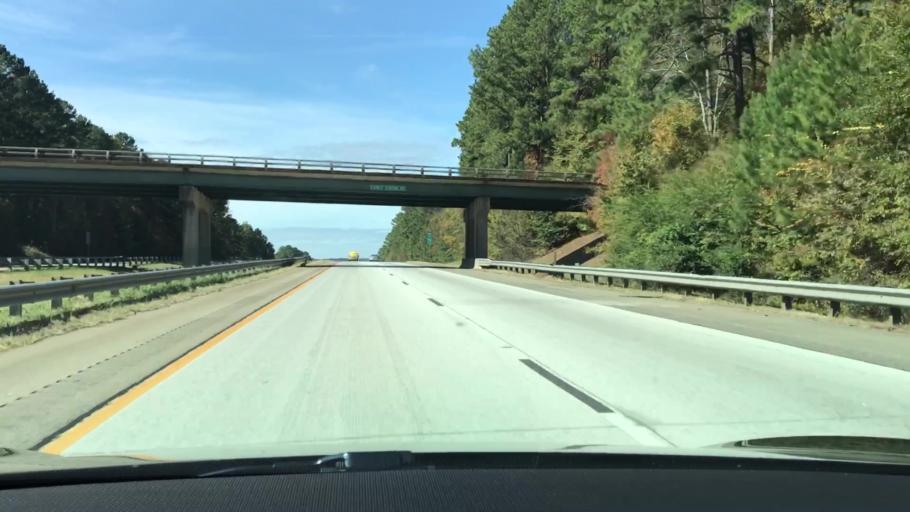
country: US
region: Georgia
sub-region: Greene County
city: Greensboro
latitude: 33.5357
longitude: -83.2515
